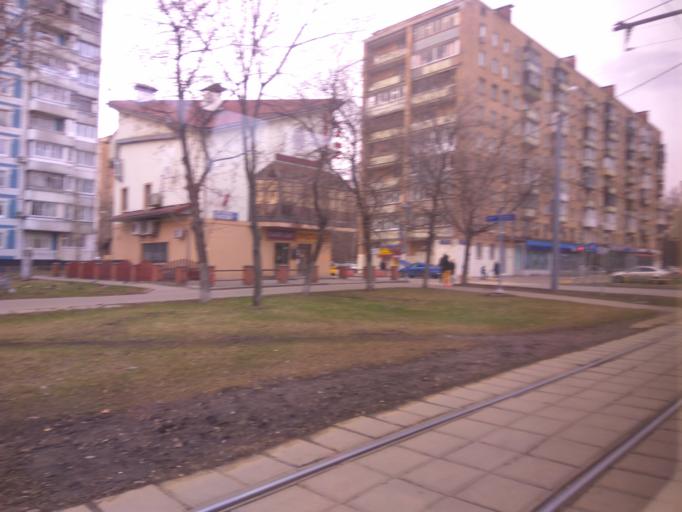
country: RU
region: Moscow
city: Leonovo
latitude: 55.8645
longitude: 37.6616
